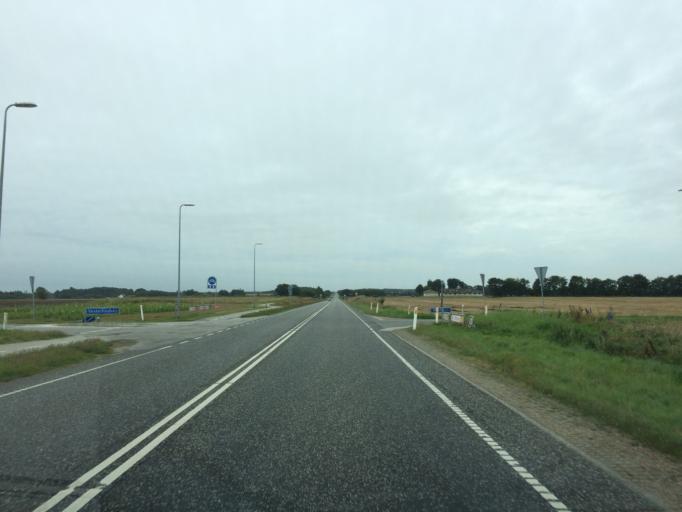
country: DK
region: Central Jutland
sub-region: Herning Kommune
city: Lind
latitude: 56.1087
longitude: 8.9401
